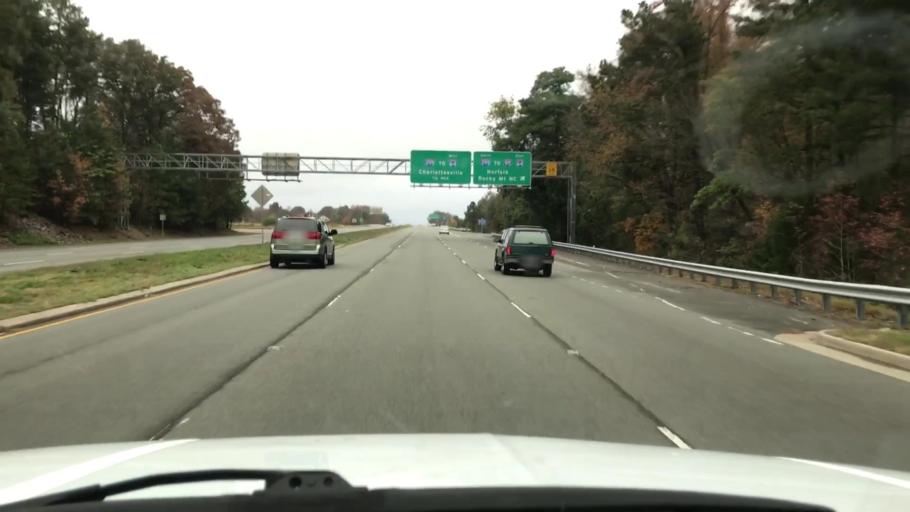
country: US
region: Virginia
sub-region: Henrico County
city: Chamberlayne
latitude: 37.6541
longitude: -77.4598
